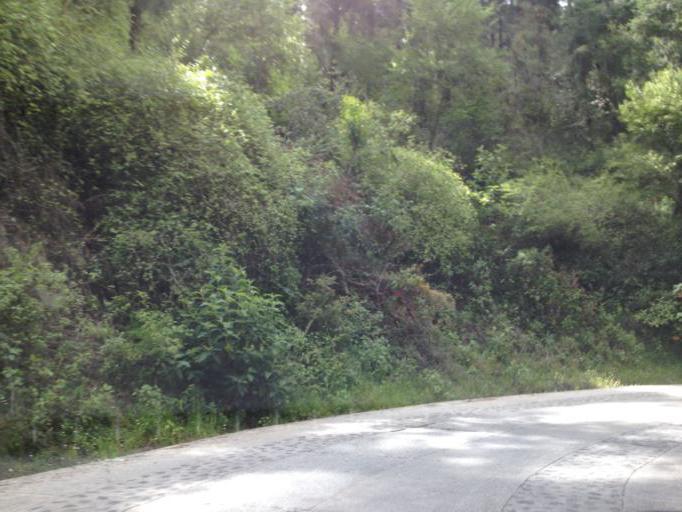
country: MX
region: Hidalgo
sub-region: Pachuca de Soto
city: San Miguel Cerezo (El Cerezo)
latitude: 20.2119
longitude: -98.6997
